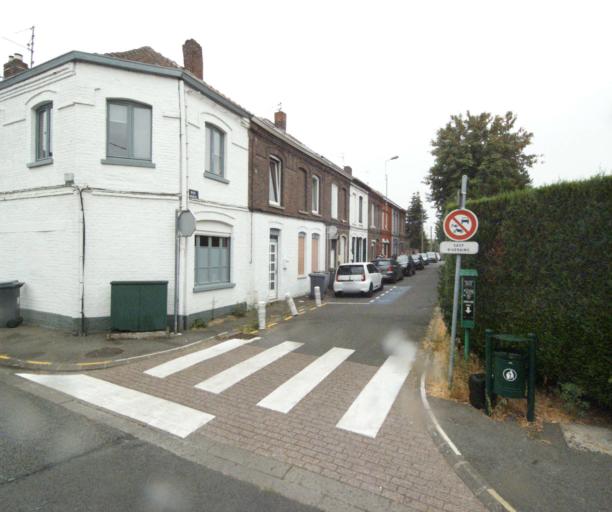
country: FR
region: Nord-Pas-de-Calais
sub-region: Departement du Nord
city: Mouvaux
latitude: 50.7034
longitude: 3.1479
